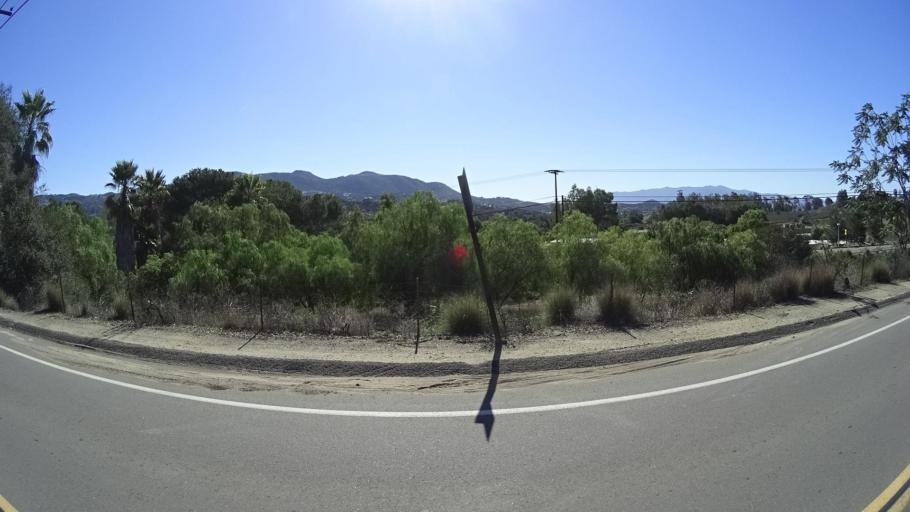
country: US
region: California
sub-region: San Diego County
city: Jamul
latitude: 32.7311
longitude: -116.8562
